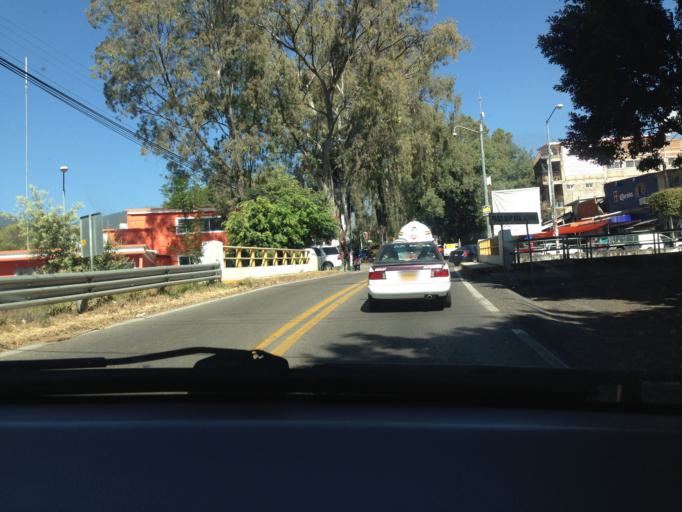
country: MX
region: Morelos
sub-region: Cuernavaca
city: Fraccionamiento Lomas de Ahuatlan
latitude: 18.9768
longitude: -99.2533
